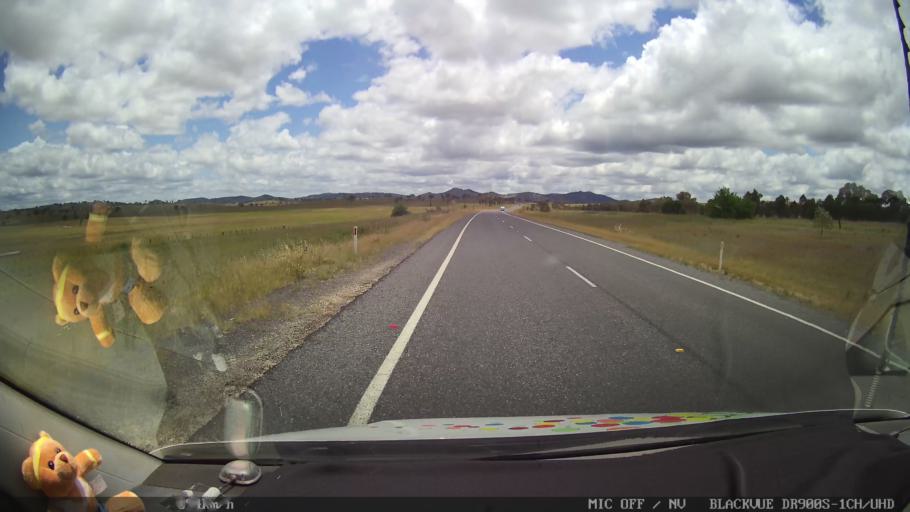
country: AU
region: New South Wales
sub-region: Glen Innes Severn
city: Glen Innes
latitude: -29.4024
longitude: 151.8729
